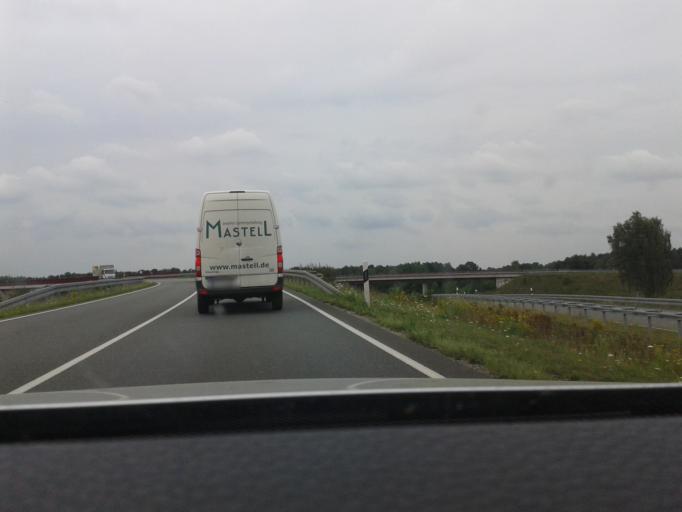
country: DE
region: Lower Saxony
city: Burgdorf
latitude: 52.4575
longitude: 9.9558
